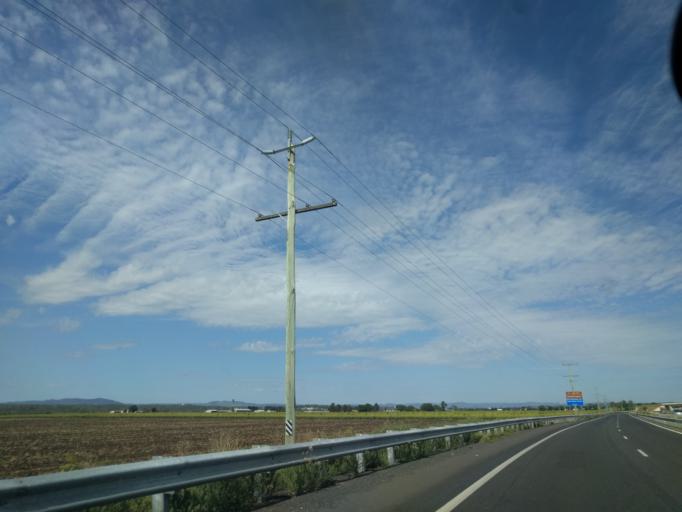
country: AU
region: Queensland
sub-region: Lockyer Valley
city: Gatton
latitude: -27.5508
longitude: 152.3238
